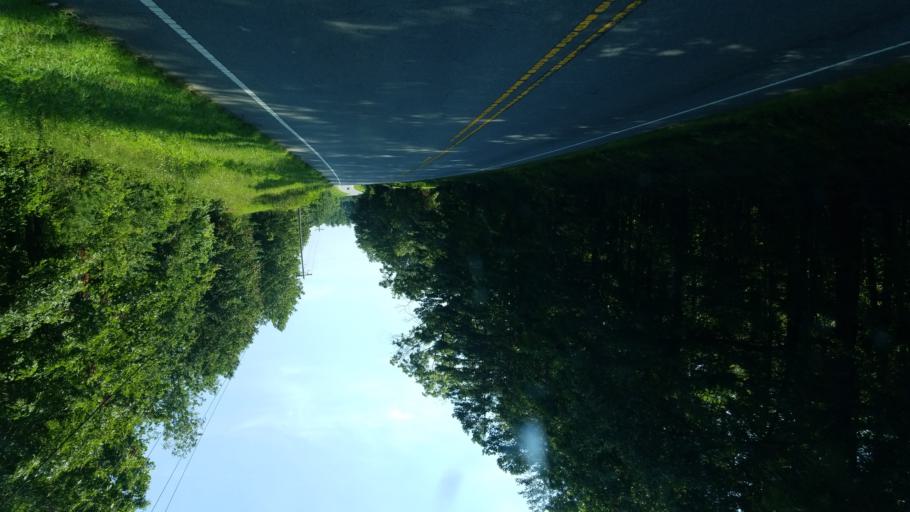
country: US
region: North Carolina
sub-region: Burke County
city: Glen Alpine
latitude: 35.8099
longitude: -81.7881
